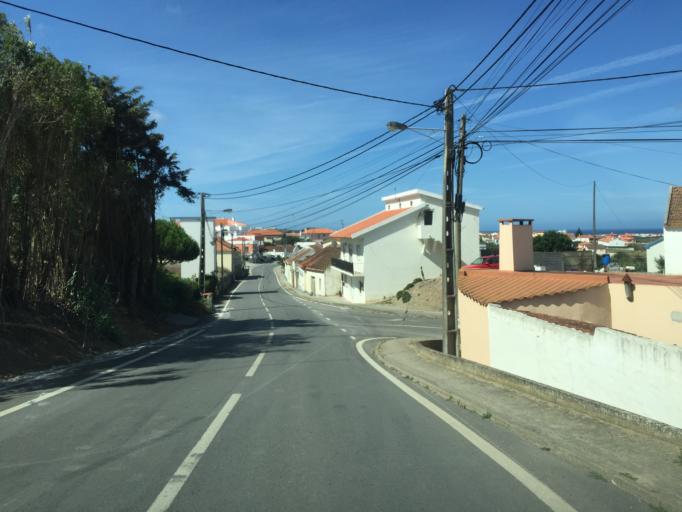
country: PT
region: Lisbon
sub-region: Lourinha
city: Lourinha
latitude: 39.2698
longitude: -9.3076
